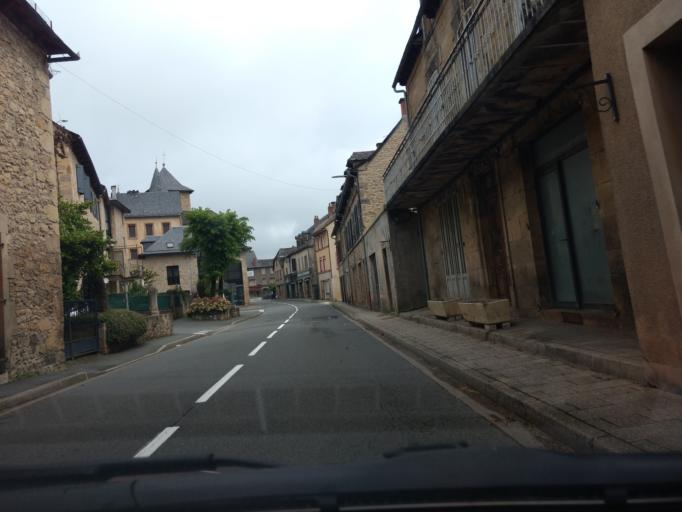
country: FR
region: Midi-Pyrenees
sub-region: Departement de l'Aveyron
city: Montbazens
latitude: 44.4763
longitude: 2.2291
